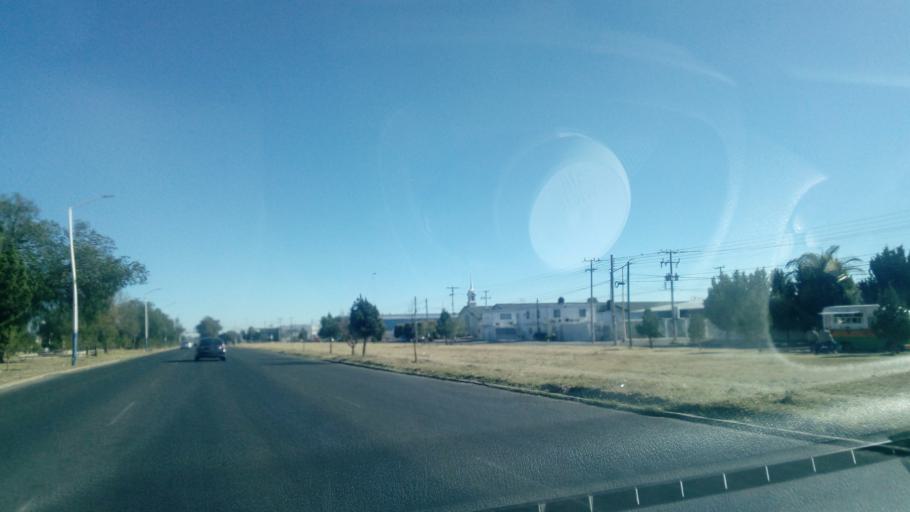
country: MX
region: Durango
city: Victoria de Durango
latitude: 24.0651
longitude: -104.6034
